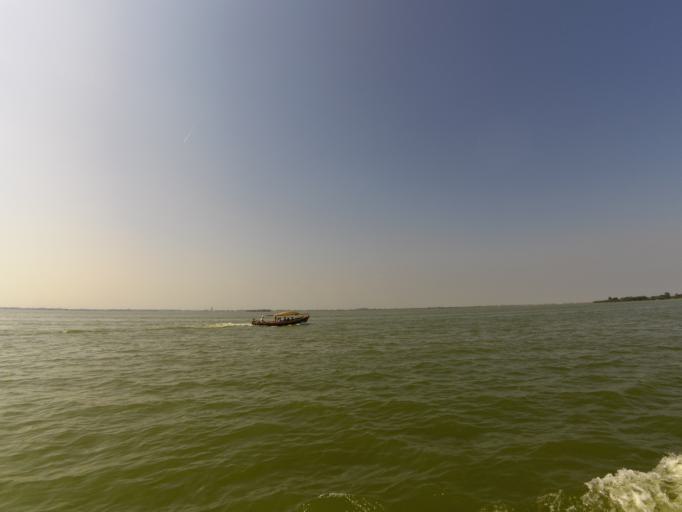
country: IT
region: Veneto
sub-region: Provincia di Venezia
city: Burano
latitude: 45.4772
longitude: 12.3920
